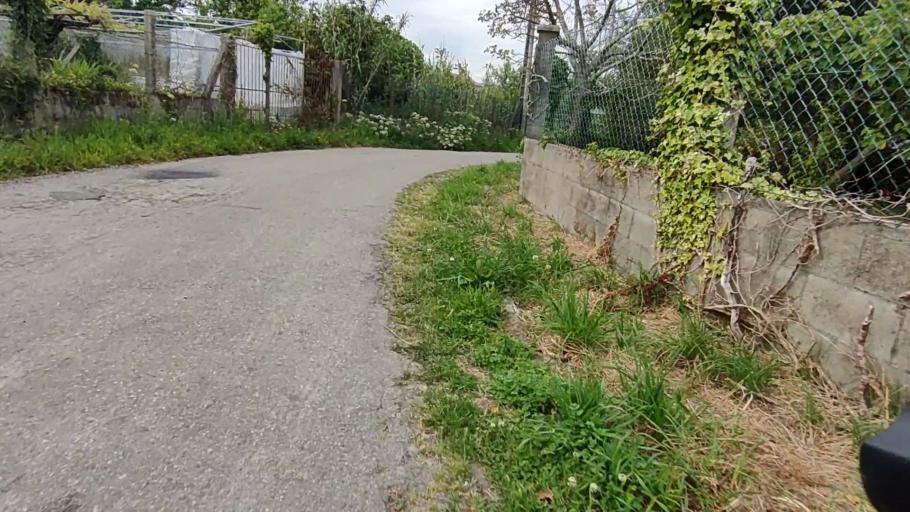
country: ES
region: Galicia
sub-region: Provincia da Coruna
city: Boiro
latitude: 42.6323
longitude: -8.8633
